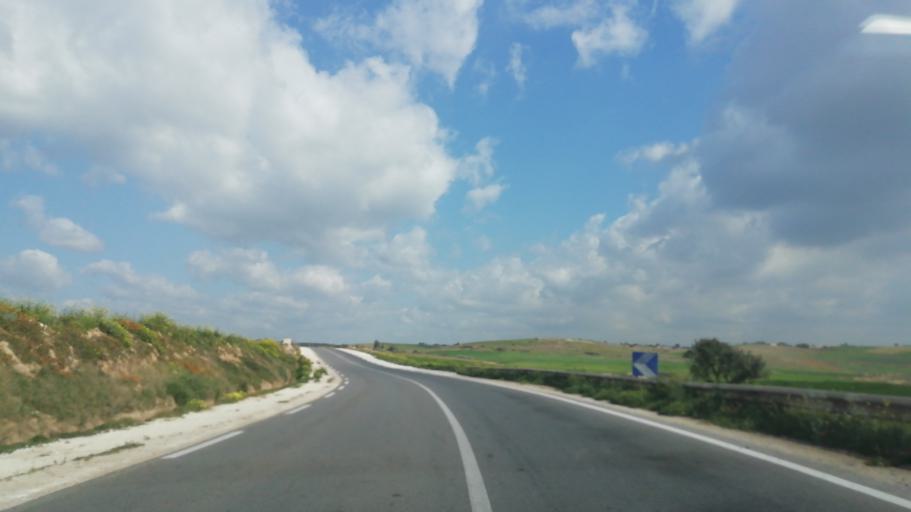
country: DZ
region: Mostaganem
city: Mostaganem
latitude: 35.6995
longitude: 0.2455
